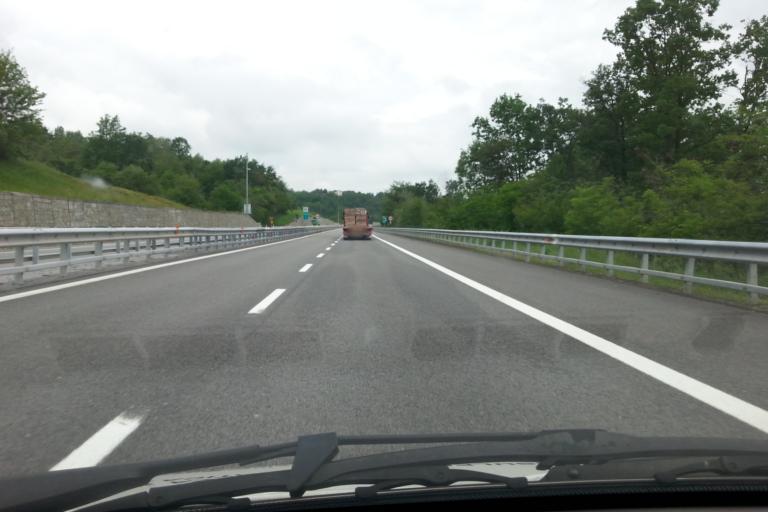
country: IT
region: Piedmont
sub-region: Provincia di Cuneo
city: Bastia Mondovi
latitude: 44.4159
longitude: 7.8975
